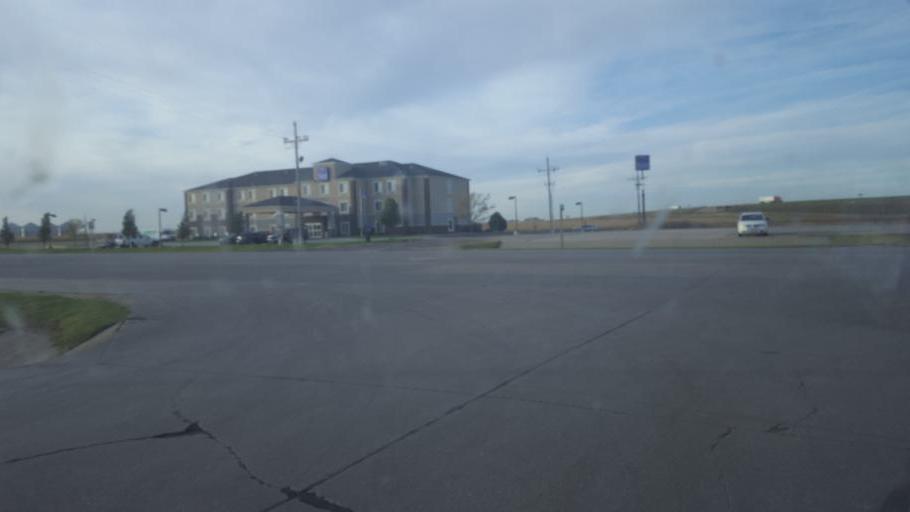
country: US
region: Kansas
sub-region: Logan County
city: Oakley
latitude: 39.1192
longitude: -100.8118
